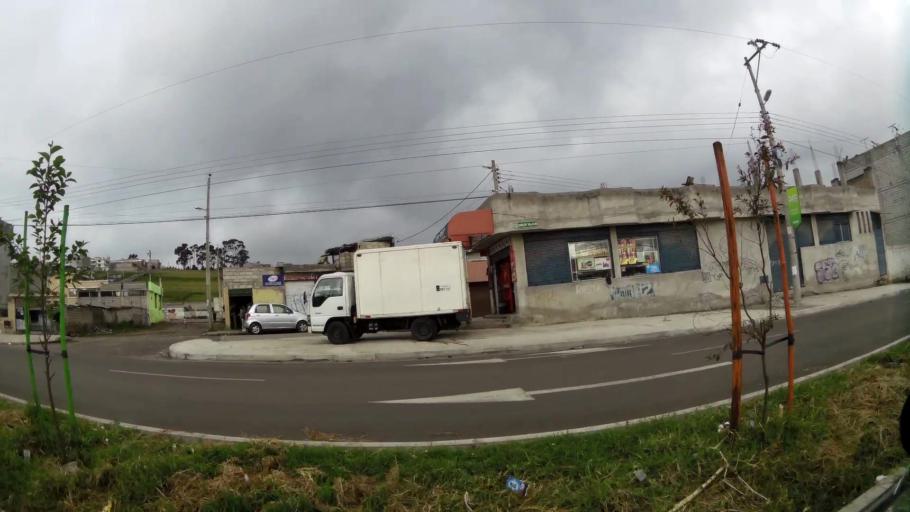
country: EC
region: Pichincha
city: Sangolqui
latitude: -0.3110
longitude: -78.5266
